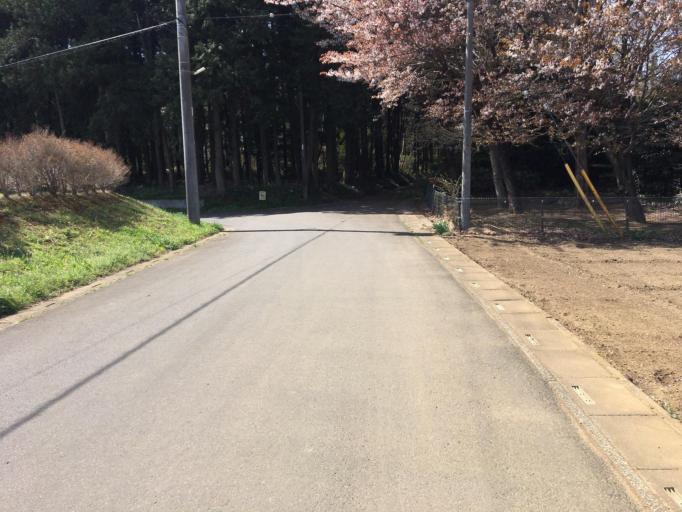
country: JP
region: Saitama
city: Sakado
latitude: 35.9591
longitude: 139.3459
